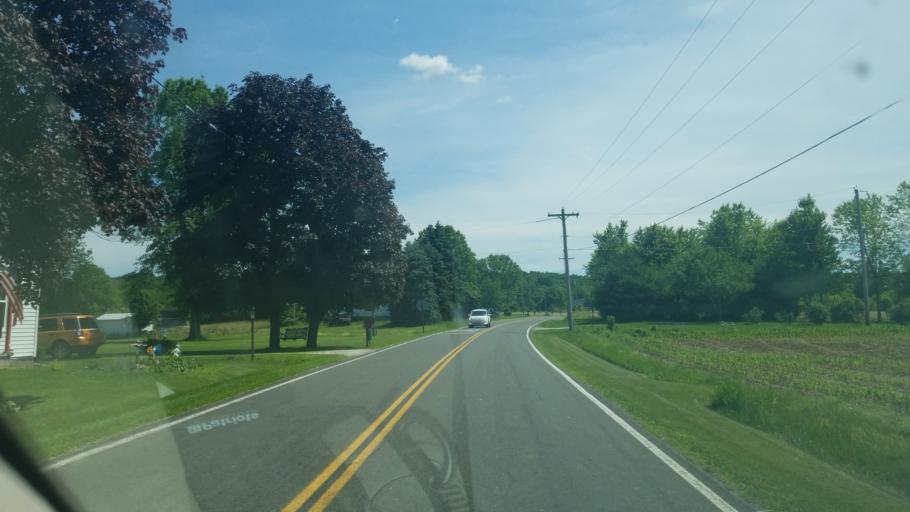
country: US
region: Ohio
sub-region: Stark County
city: Brewster
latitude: 40.7112
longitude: -81.5726
